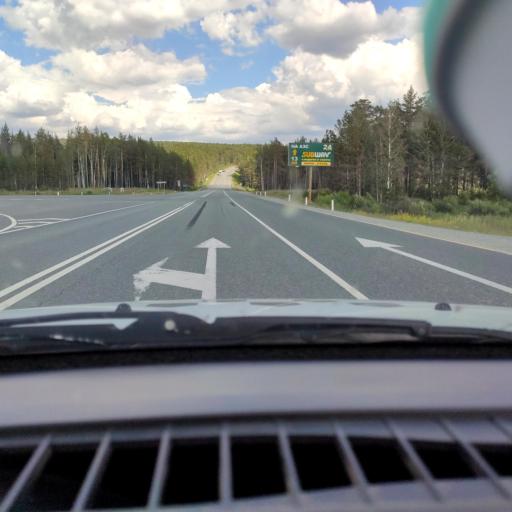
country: RU
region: Chelyabinsk
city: Zlatoust
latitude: 55.0557
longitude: 59.6959
